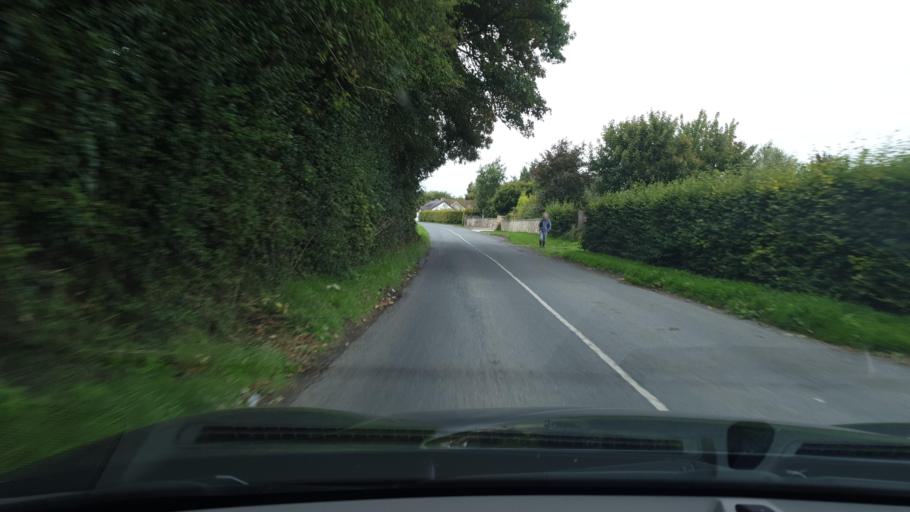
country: IE
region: Leinster
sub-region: Kildare
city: Kilcock
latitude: 53.4049
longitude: -6.6632
